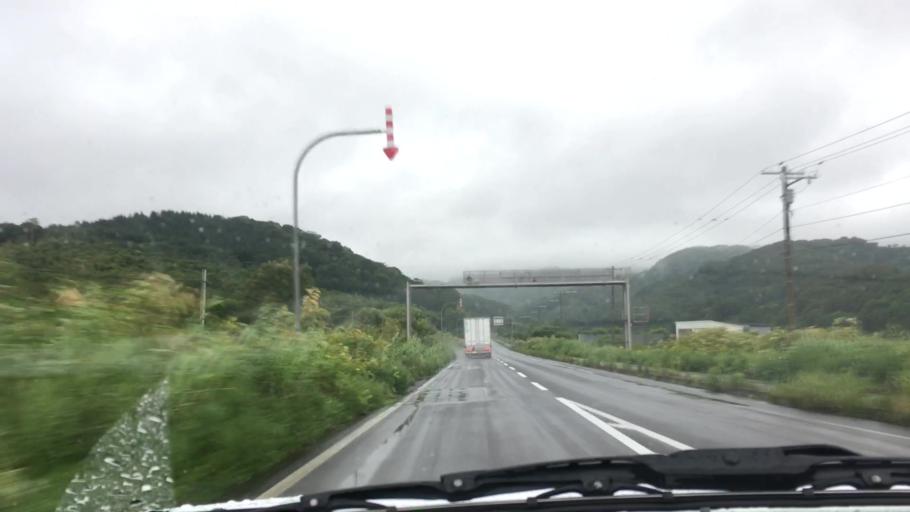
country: JP
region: Hokkaido
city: Niseko Town
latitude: 42.5993
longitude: 140.6335
